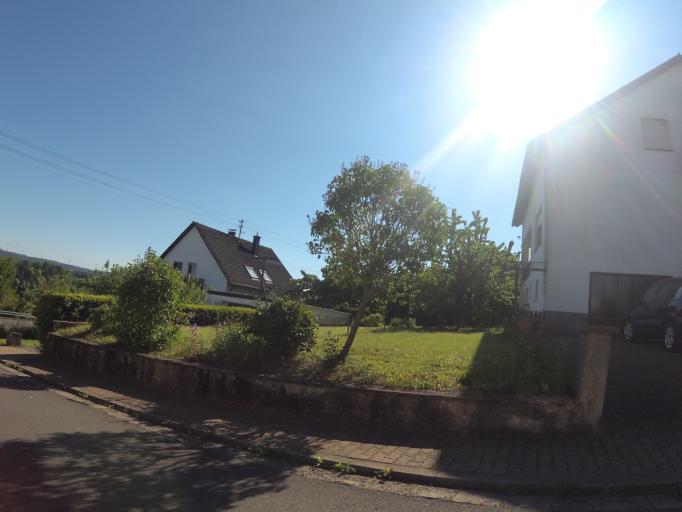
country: DE
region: Saarland
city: Orscholz
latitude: 49.4847
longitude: 6.5430
